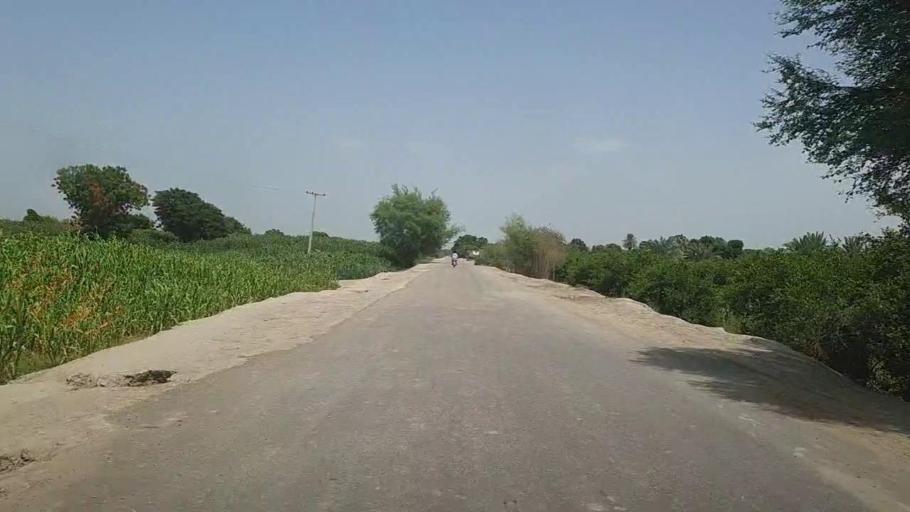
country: PK
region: Sindh
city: Pad Idan
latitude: 26.8430
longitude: 68.3353
